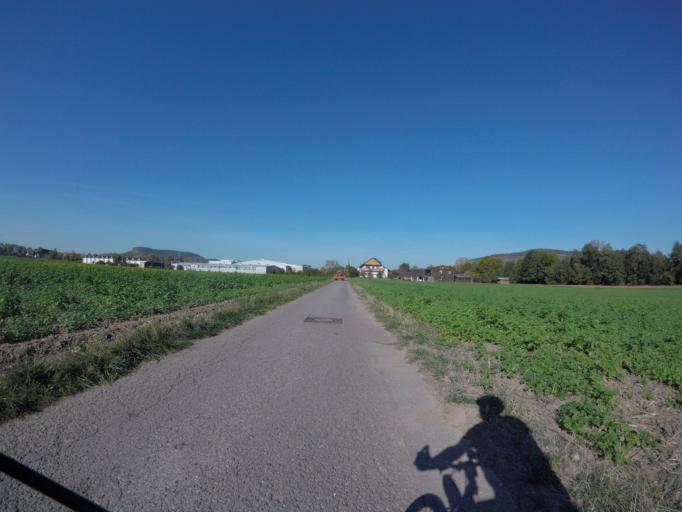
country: DE
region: Baden-Wuerttemberg
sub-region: Regierungsbezirk Stuttgart
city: Sersheim
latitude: 48.9747
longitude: 8.9958
